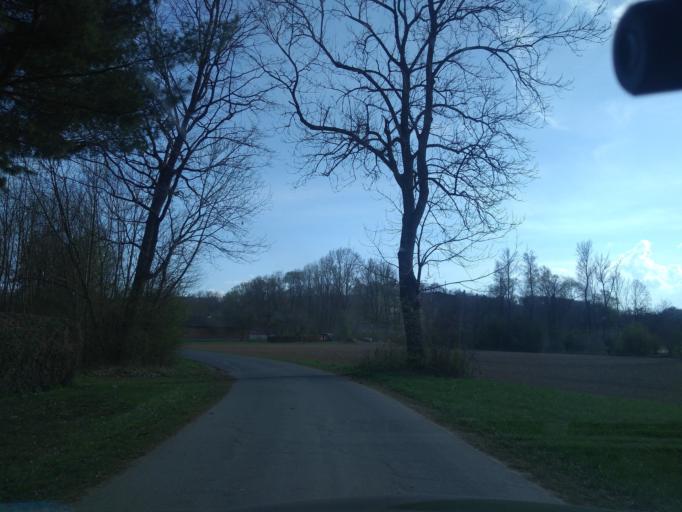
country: SI
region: Sentilj
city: Selnica ob Muri
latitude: 46.7035
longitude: 15.7282
